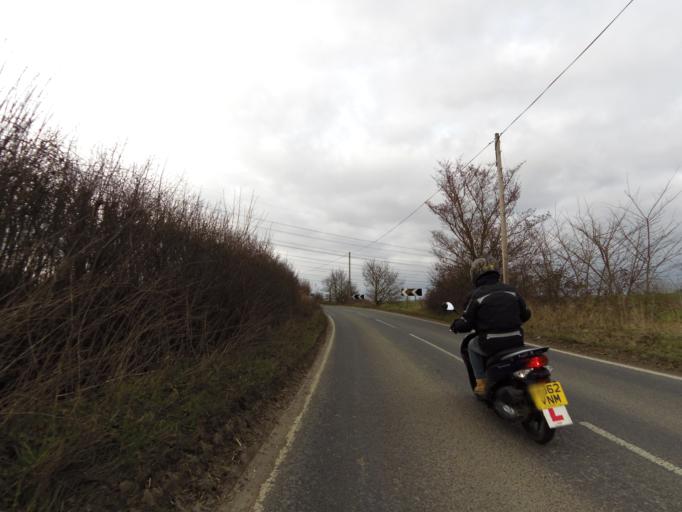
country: GB
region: England
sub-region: Suffolk
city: Ipswich
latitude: 52.0946
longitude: 1.1557
